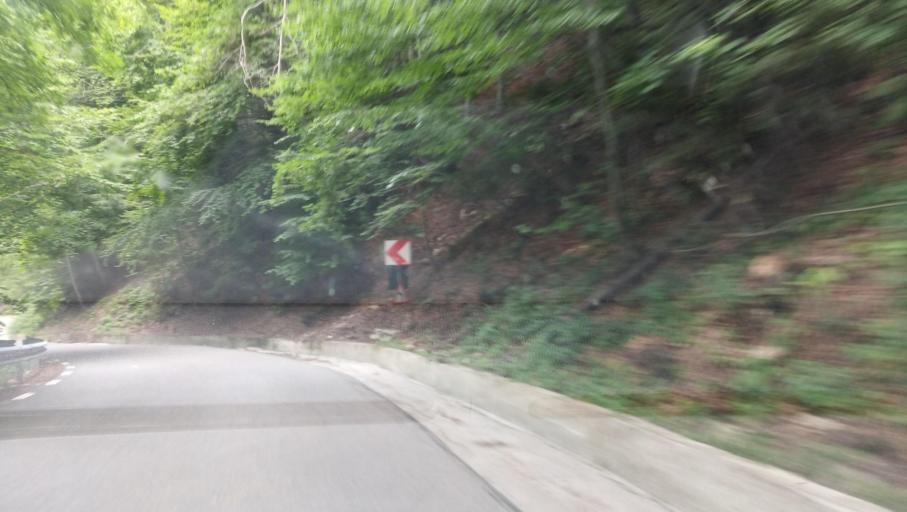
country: RO
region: Prahova
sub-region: Oras Sinaia
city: Sinaia
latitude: 45.3235
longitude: 25.4984
